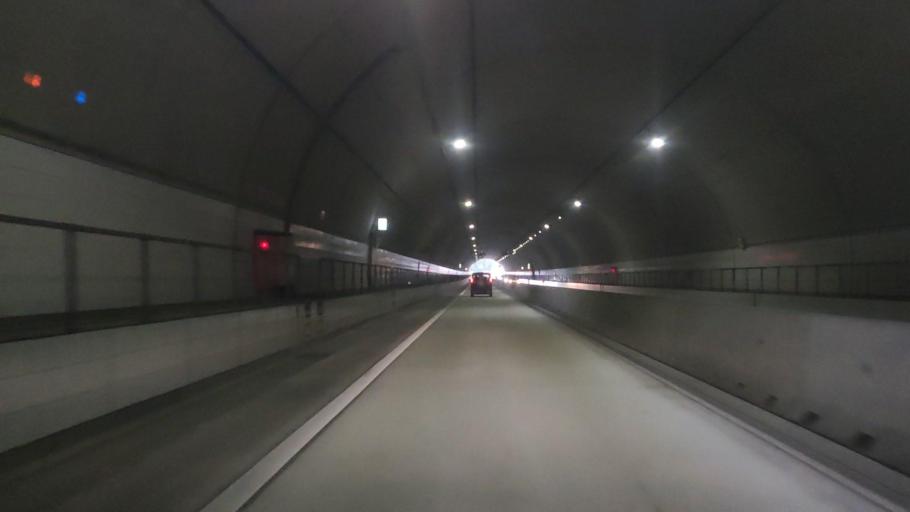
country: JP
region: Kumamoto
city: Ozu
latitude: 32.9018
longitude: 130.9422
